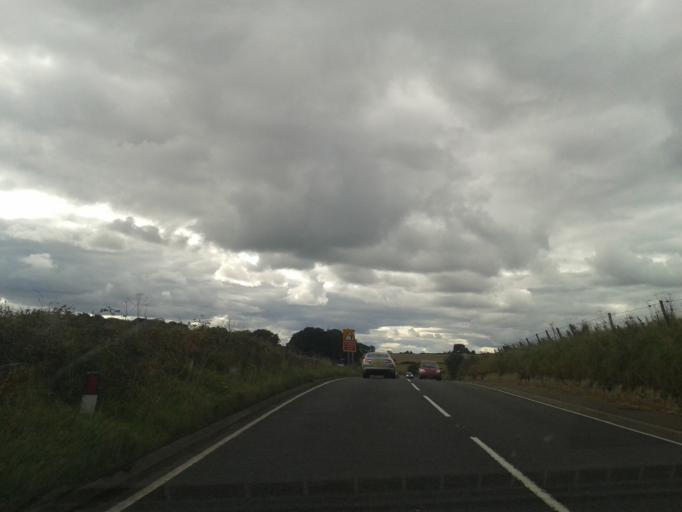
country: GB
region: Scotland
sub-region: Fife
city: Ceres
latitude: 56.3347
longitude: -2.9715
